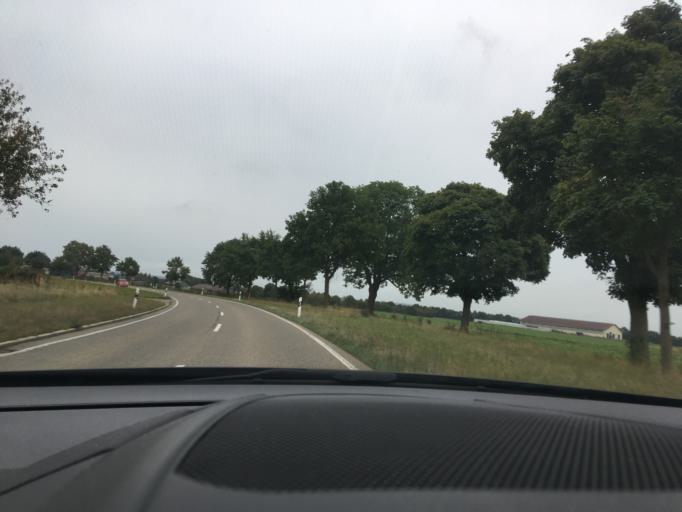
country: DE
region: Baden-Wuerttemberg
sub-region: Tuebingen Region
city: Kirchdorf
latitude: 48.0785
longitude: 10.1114
